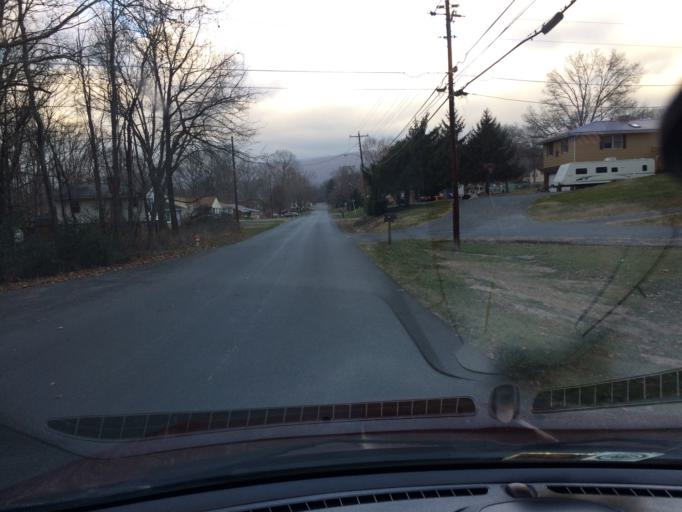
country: US
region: Virginia
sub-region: Alleghany County
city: Clifton Forge
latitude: 37.8271
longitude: -79.8176
